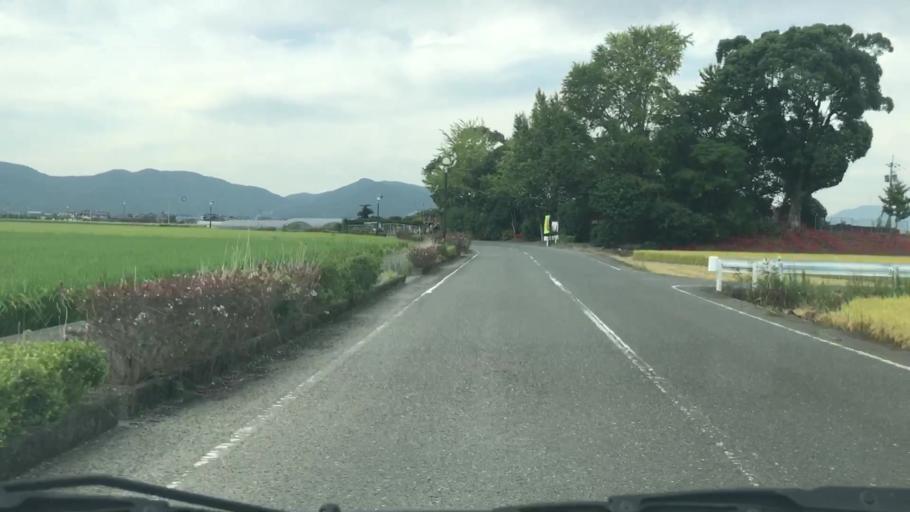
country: JP
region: Saga Prefecture
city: Kashima
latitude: 33.1451
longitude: 130.1439
